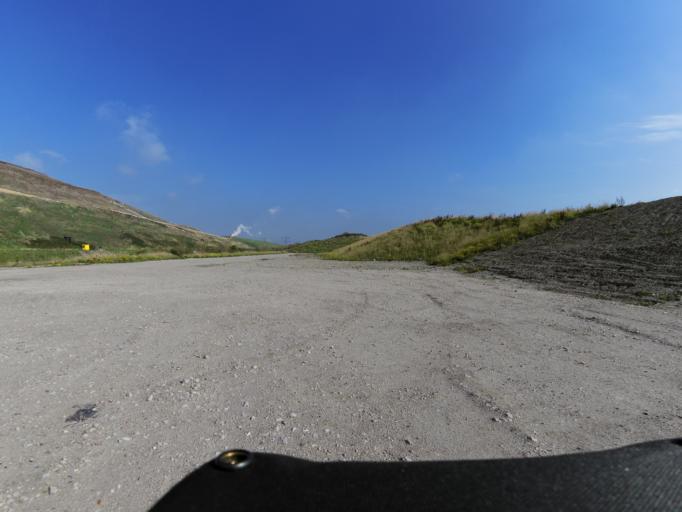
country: NL
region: South Holland
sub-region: Gemeente Goeree-Overflakkee
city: Goedereede
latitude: 51.9221
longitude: 4.0228
